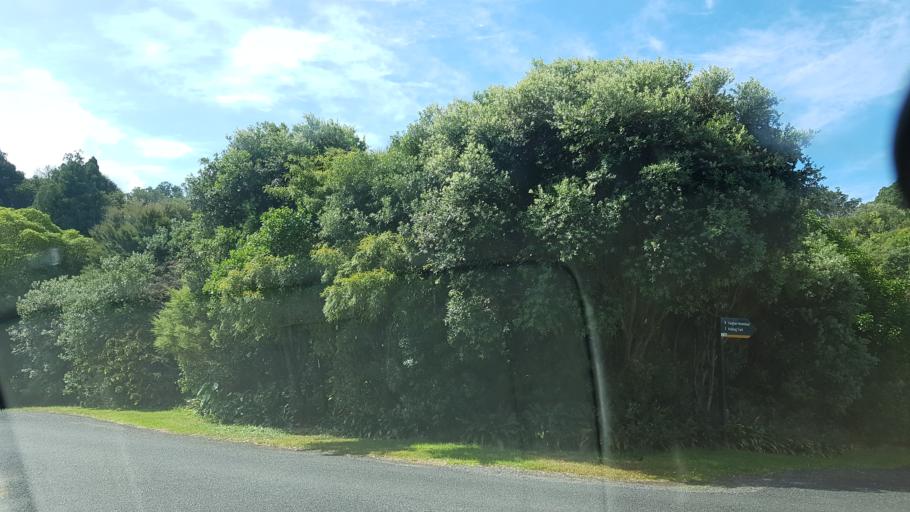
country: NZ
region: Auckland
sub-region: Auckland
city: Rothesay Bay
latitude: -36.6810
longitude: 174.7456
